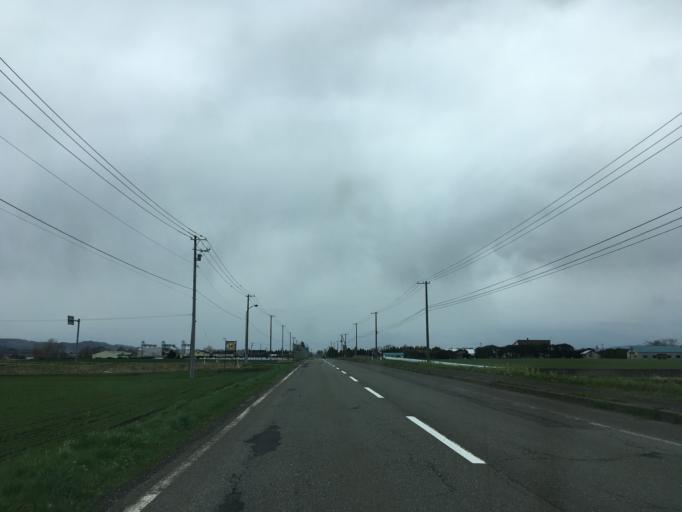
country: JP
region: Hokkaido
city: Chitose
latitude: 42.9275
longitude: 141.8076
